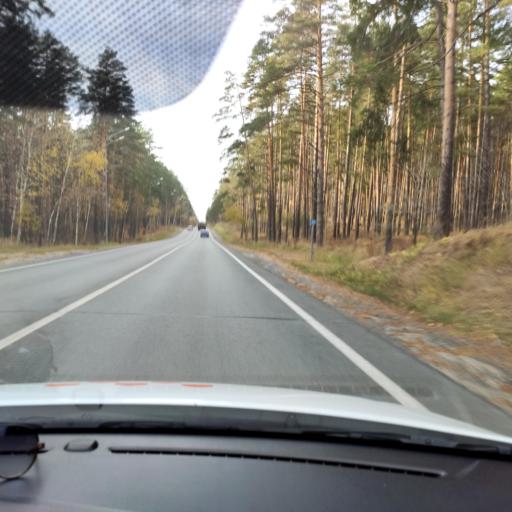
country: RU
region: Tatarstan
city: Verkhniy Uslon
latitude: 55.6371
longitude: 49.0563
